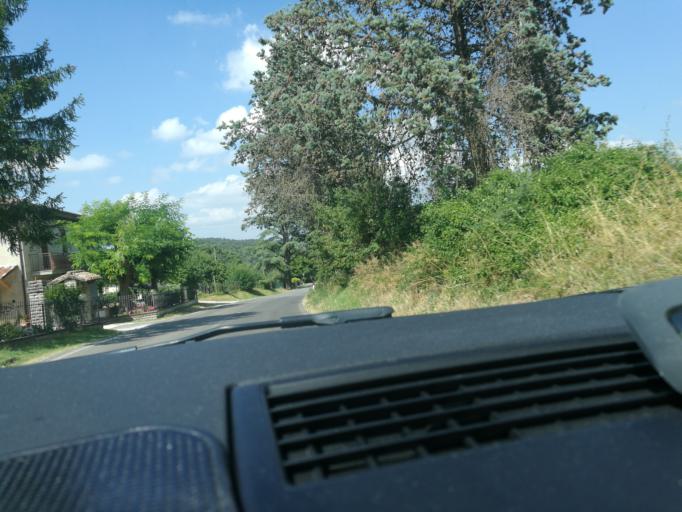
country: IT
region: Umbria
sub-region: Provincia di Terni
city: Fornole
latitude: 42.5610
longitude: 12.4425
